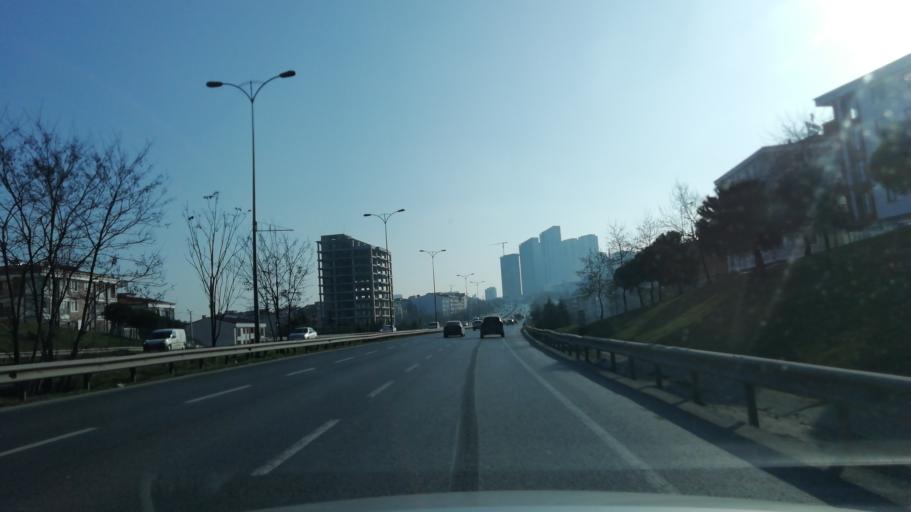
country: TR
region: Istanbul
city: Esenyurt
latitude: 41.0427
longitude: 28.6904
